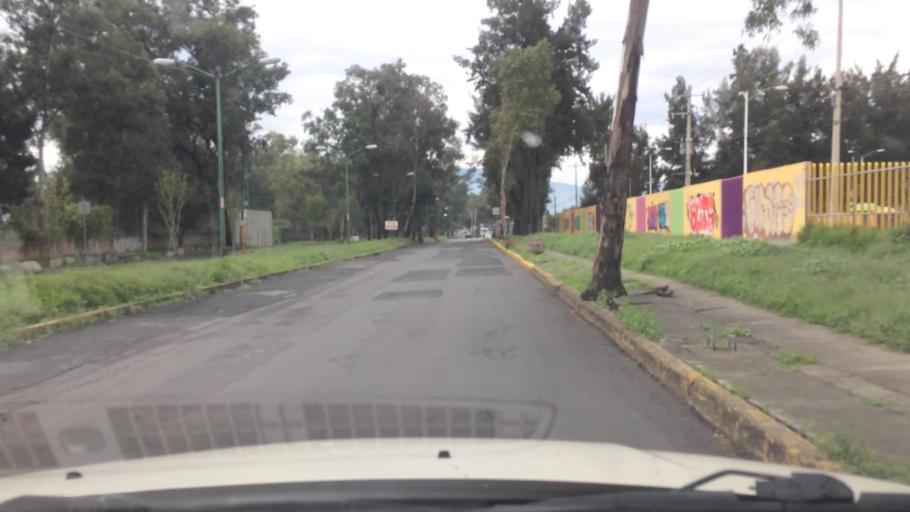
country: MX
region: Mexico City
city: Iztapalapa
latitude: 19.3164
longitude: -99.0997
